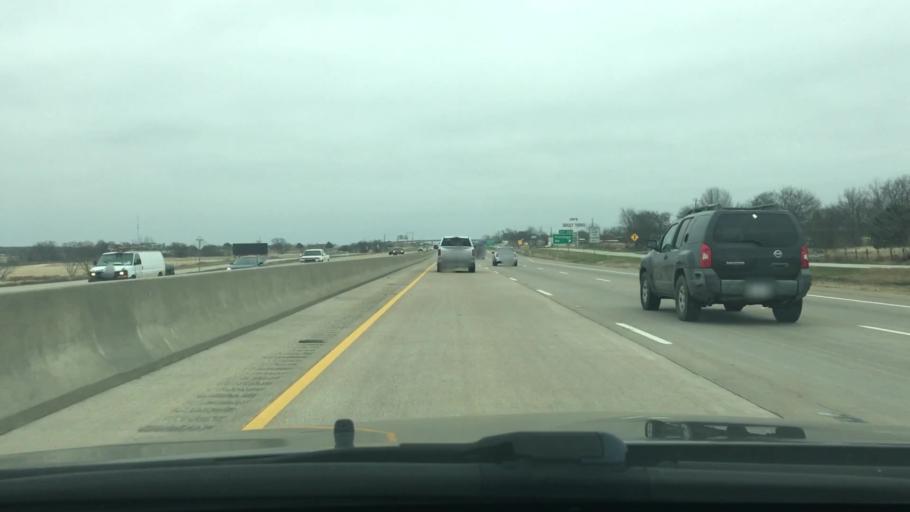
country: US
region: Texas
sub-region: Ellis County
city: Ennis
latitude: 32.2652
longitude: -96.5079
